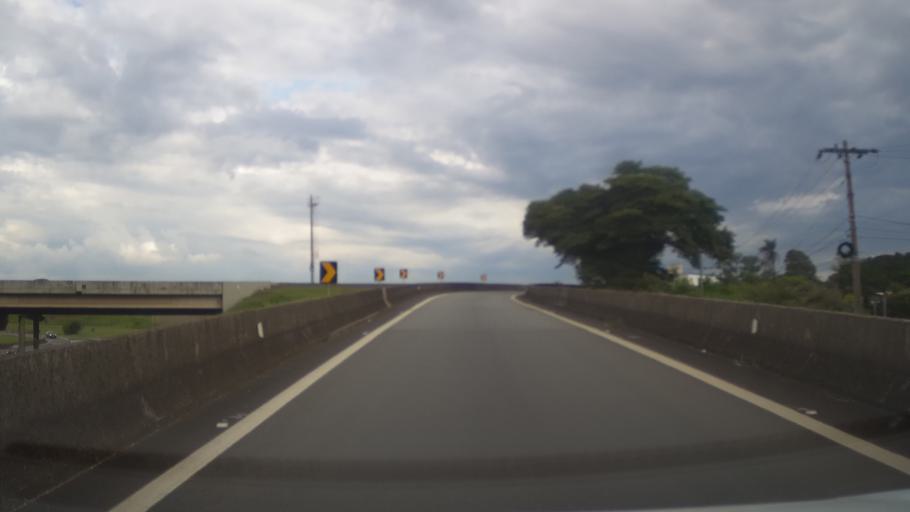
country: BR
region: Sao Paulo
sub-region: Campinas
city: Campinas
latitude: -22.8960
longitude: -47.1112
